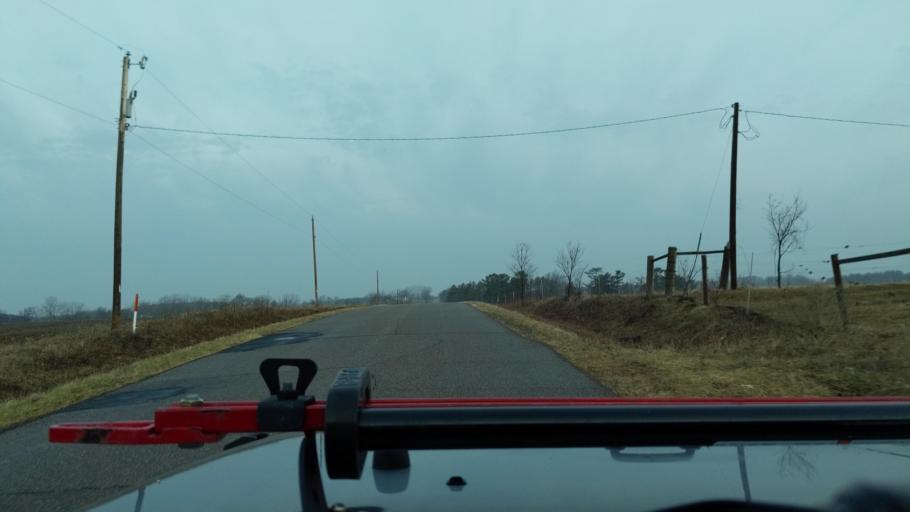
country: US
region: Wisconsin
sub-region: Saint Croix County
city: Baldwin
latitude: 44.9342
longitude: -92.3993
